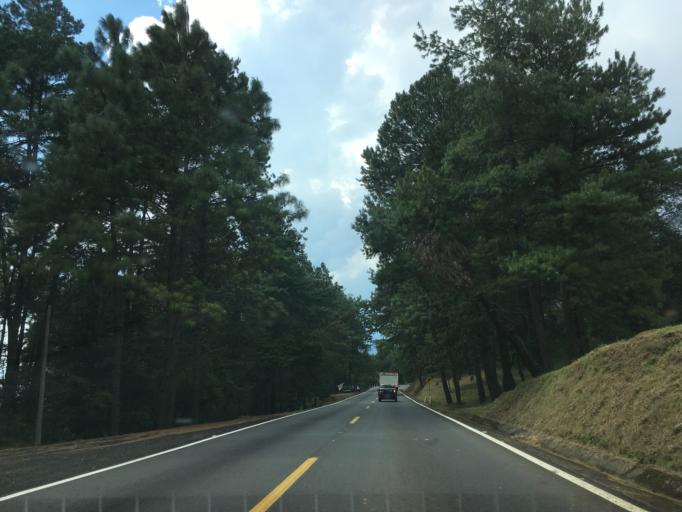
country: MX
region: Michoacan
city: Tingambato
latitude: 19.4954
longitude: -101.8244
